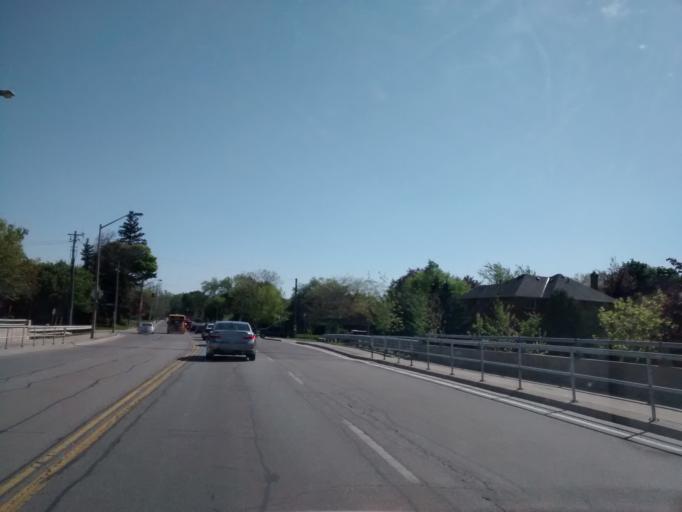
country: CA
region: Ontario
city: Oakville
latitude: 43.3919
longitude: -79.7142
